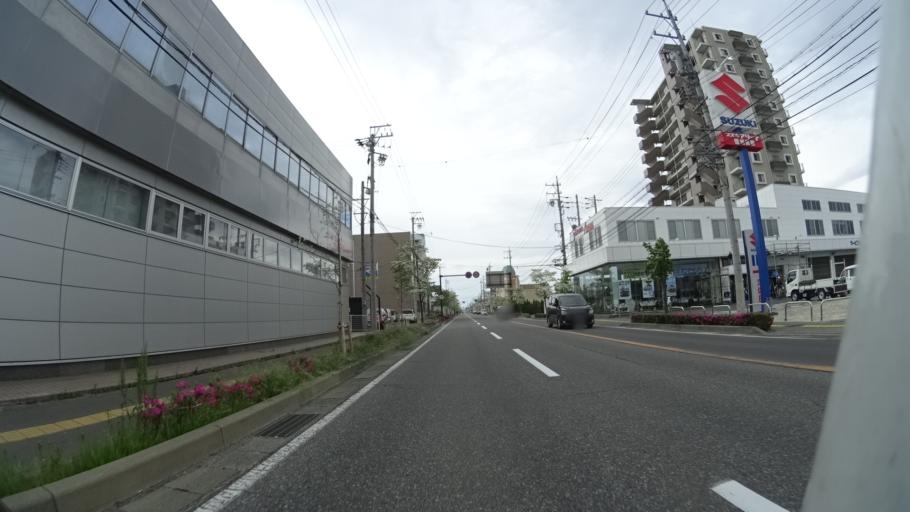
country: JP
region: Nagano
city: Nagano-shi
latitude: 36.6061
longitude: 138.1640
